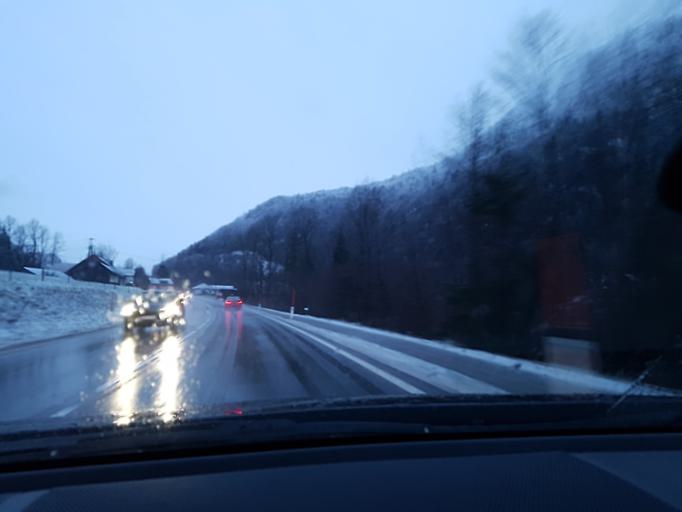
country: AT
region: Upper Austria
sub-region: Politischer Bezirk Gmunden
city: Bad Ischl
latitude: 47.6820
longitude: 13.6206
